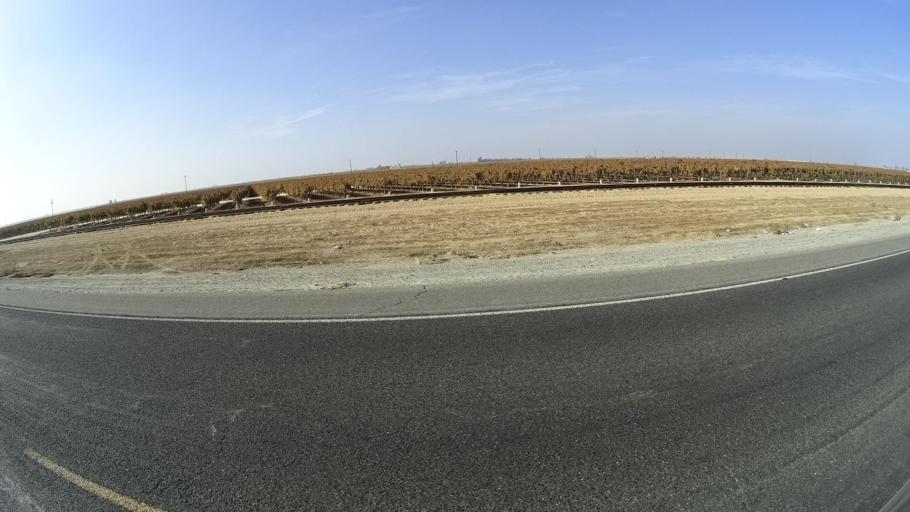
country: US
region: California
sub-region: Kern County
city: McFarland
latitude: 35.6642
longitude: -119.1928
